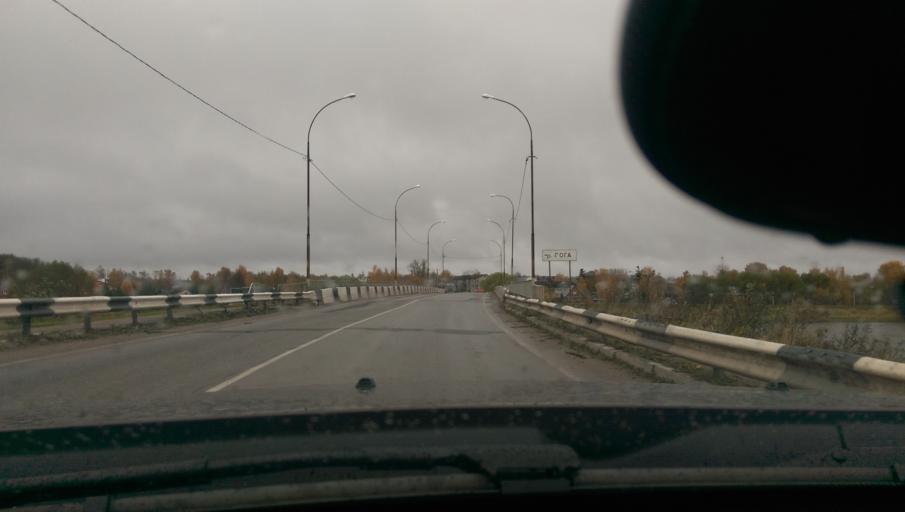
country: RU
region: Jaroslavl
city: Poshekhon'ye
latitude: 58.5067
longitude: 39.1322
